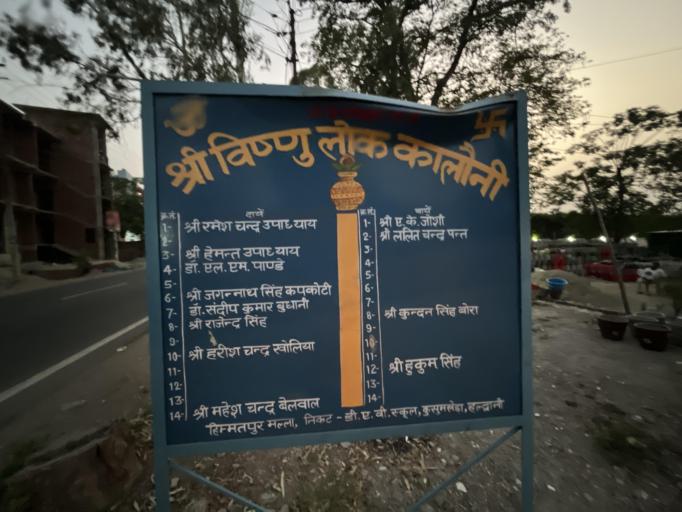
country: IN
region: Uttarakhand
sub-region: Naini Tal
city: Haldwani
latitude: 29.2196
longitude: 79.4934
